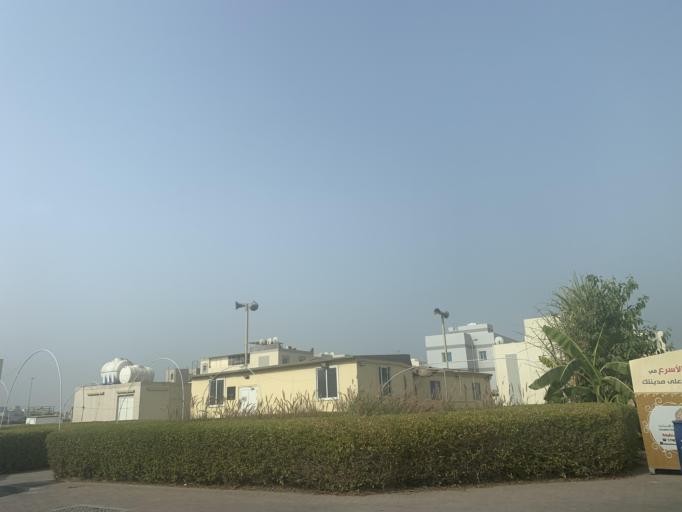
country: BH
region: Manama
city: Jidd Hafs
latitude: 26.2330
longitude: 50.4510
